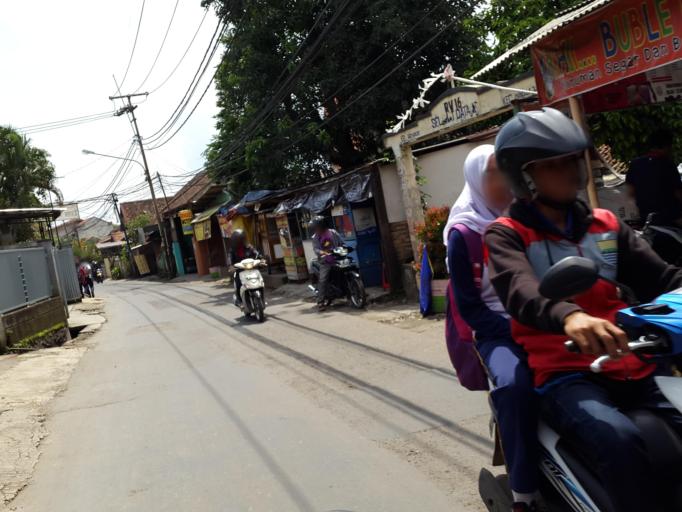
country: ID
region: West Java
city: Bandung
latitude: -6.8959
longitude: 107.6586
